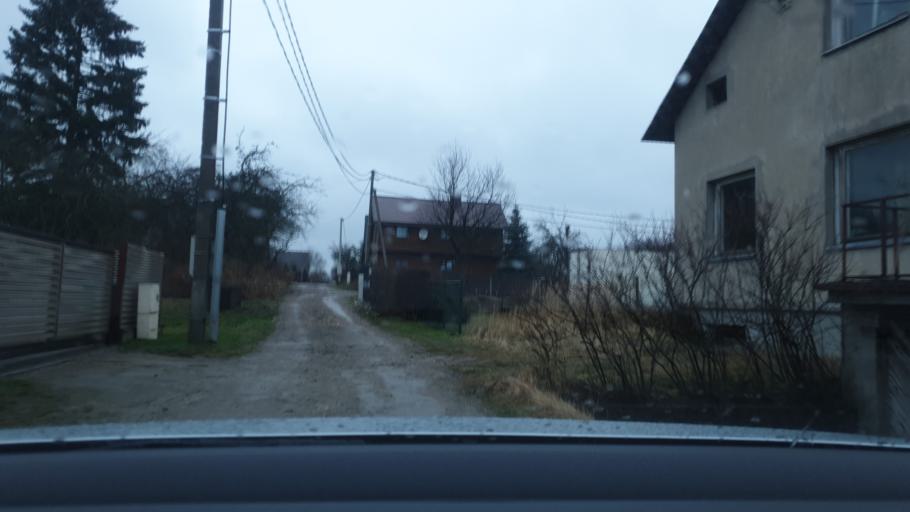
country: LT
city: Skaidiskes
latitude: 54.7052
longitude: 25.4033
